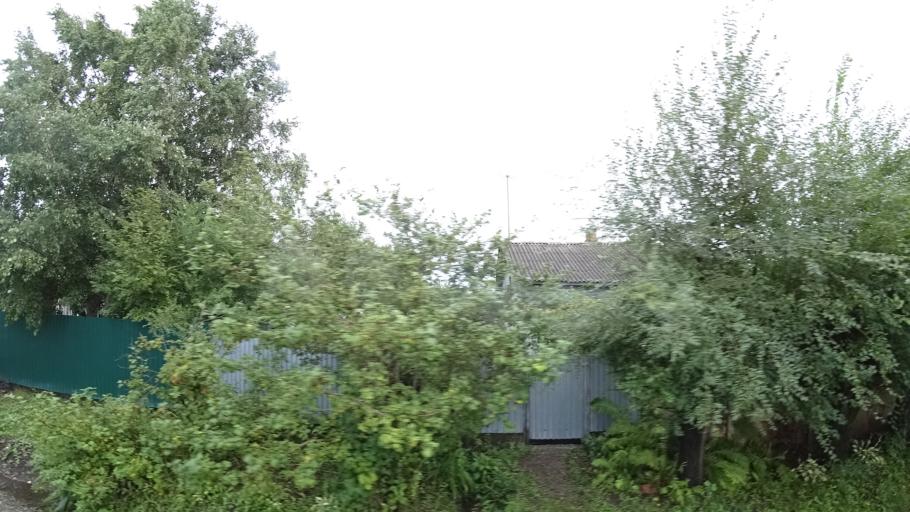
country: RU
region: Primorskiy
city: Monastyrishche
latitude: 44.1913
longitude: 132.4221
